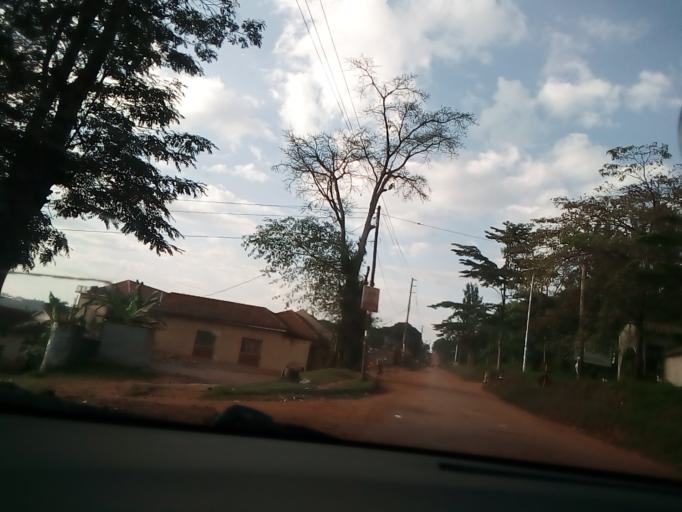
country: UG
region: Central Region
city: Masaka
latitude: -0.3493
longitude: 31.7395
